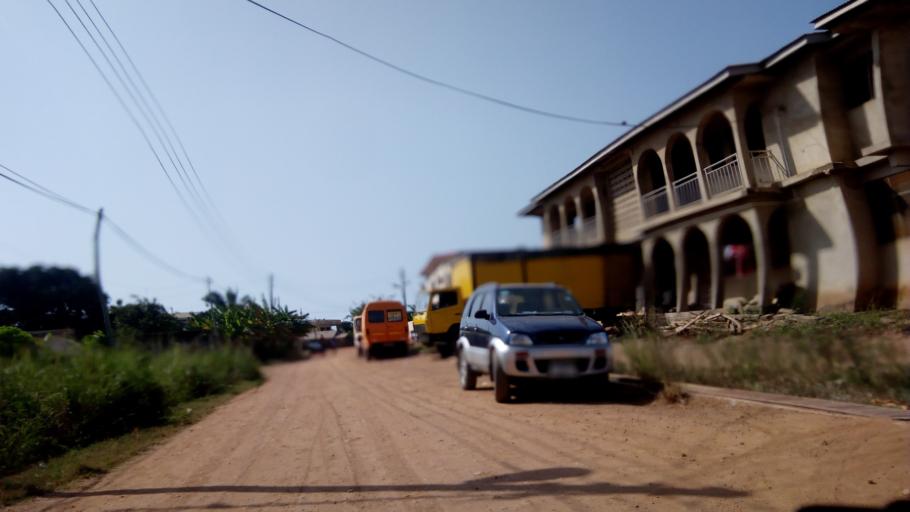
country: GH
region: Central
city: Cape Coast
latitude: 5.1180
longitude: -1.2702
